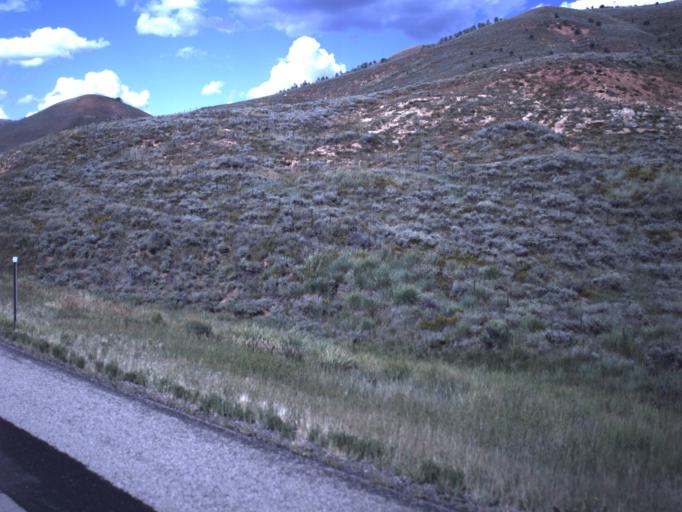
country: US
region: Utah
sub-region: Wasatch County
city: Heber
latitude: 40.2019
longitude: -111.1050
